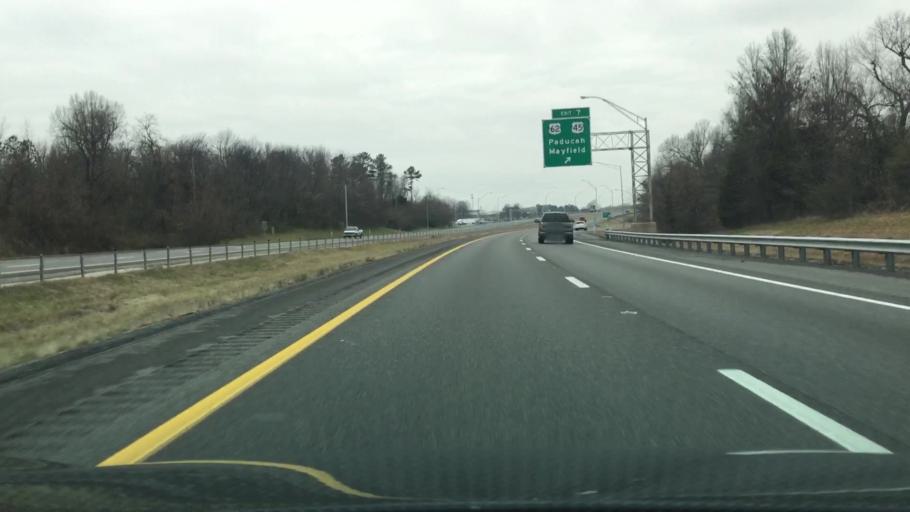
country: US
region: Kentucky
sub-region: McCracken County
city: Hendron
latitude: 37.0468
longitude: -88.6472
